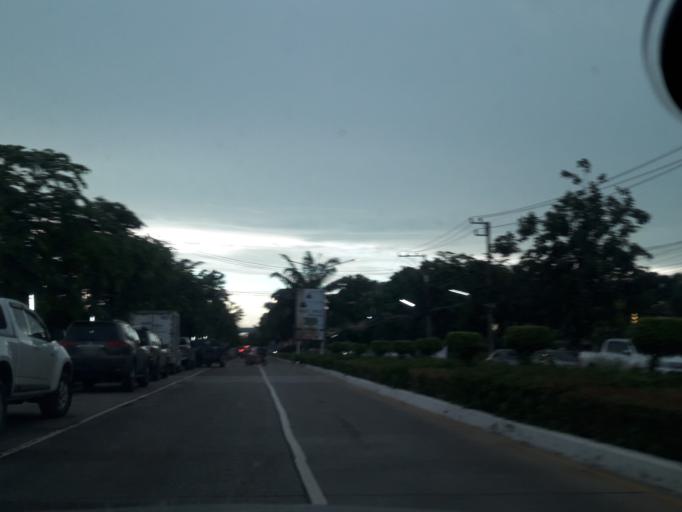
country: TH
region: Pathum Thani
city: Lam Luk Ka
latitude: 13.9348
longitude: 100.7398
